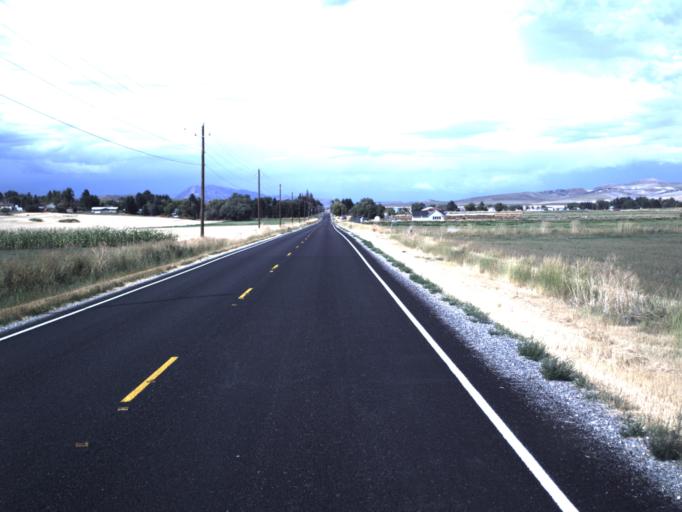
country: US
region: Utah
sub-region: Cache County
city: Benson
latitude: 41.9071
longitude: -112.0455
